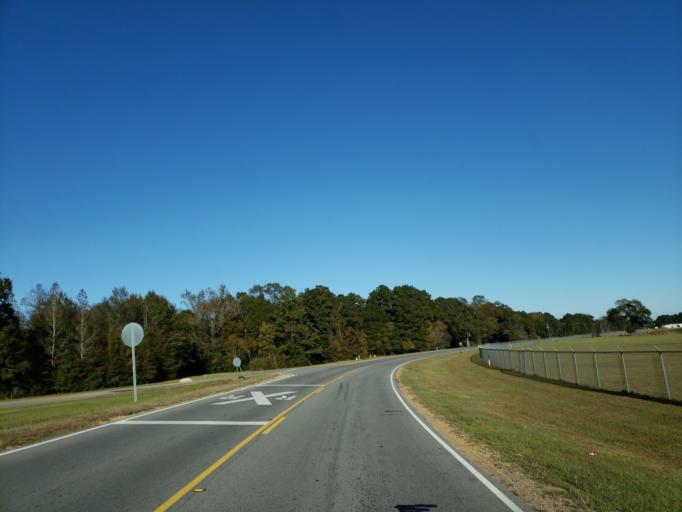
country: US
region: Mississippi
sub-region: Forrest County
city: Hattiesburg
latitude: 31.2725
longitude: -89.2616
